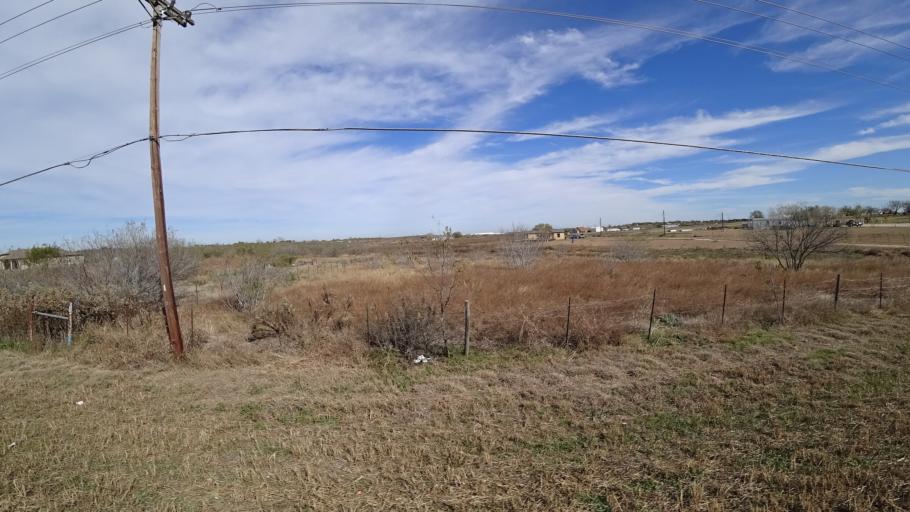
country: US
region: Texas
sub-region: Travis County
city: Onion Creek
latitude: 30.1019
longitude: -97.6872
